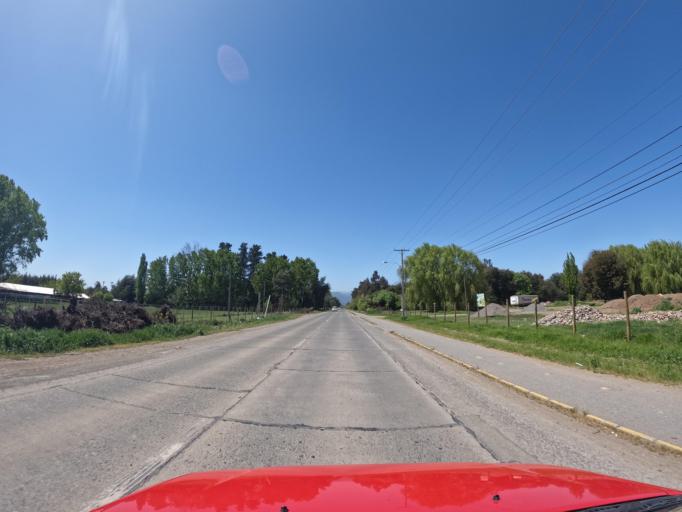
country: CL
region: Maule
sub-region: Provincia de Linares
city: Linares
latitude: -35.8316
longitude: -71.5229
